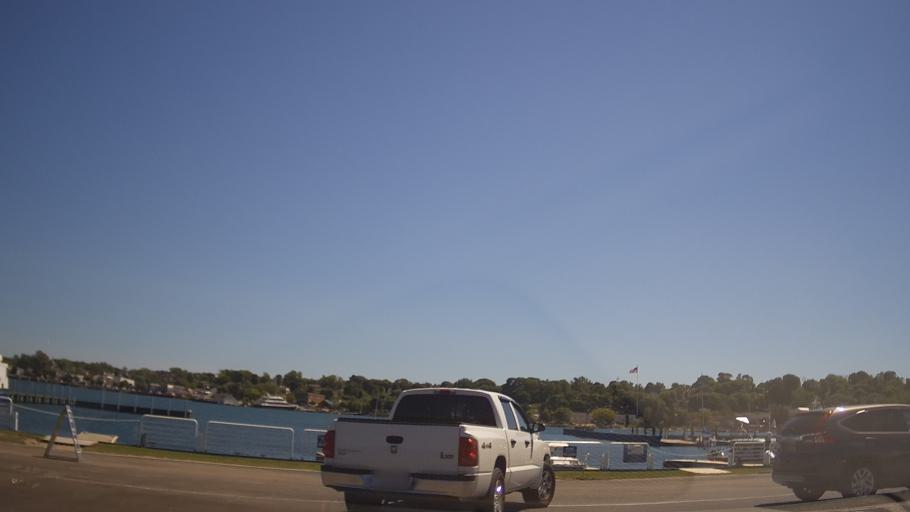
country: US
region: Michigan
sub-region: Mackinac County
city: Saint Ignace
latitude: 45.8744
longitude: -84.7289
